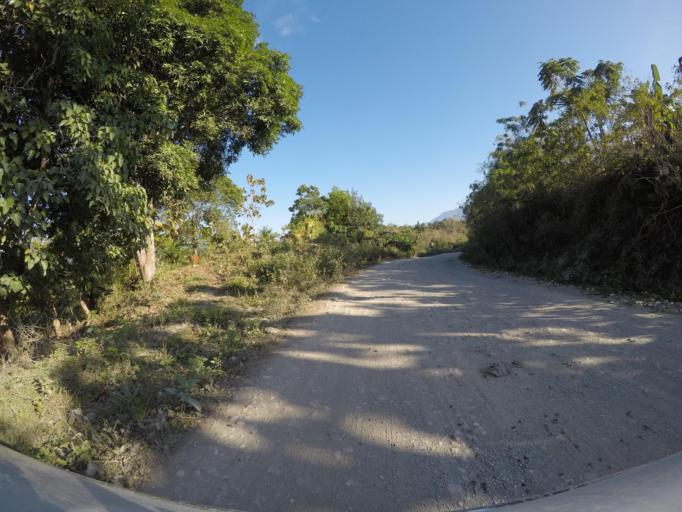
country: TL
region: Viqueque
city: Viqueque
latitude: -8.8711
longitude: 126.3437
